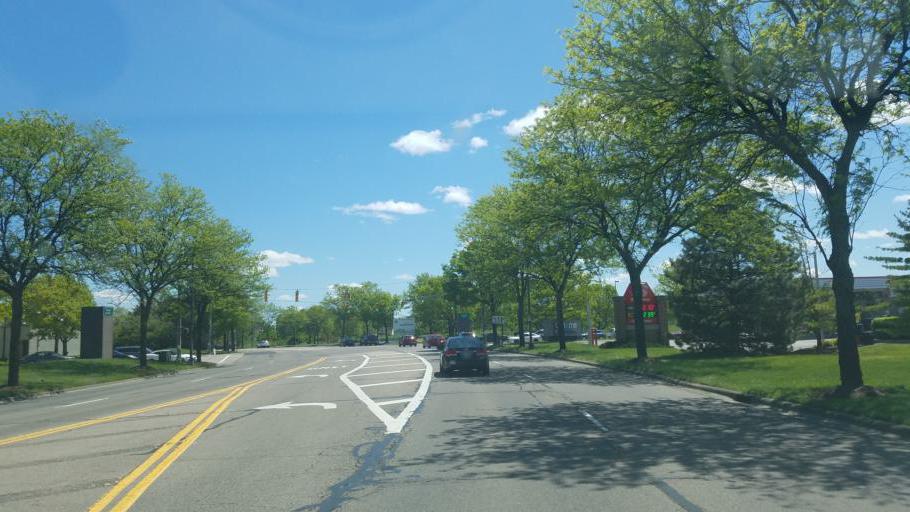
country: US
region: Ohio
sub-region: Franklin County
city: Hilliard
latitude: 40.0281
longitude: -83.1171
